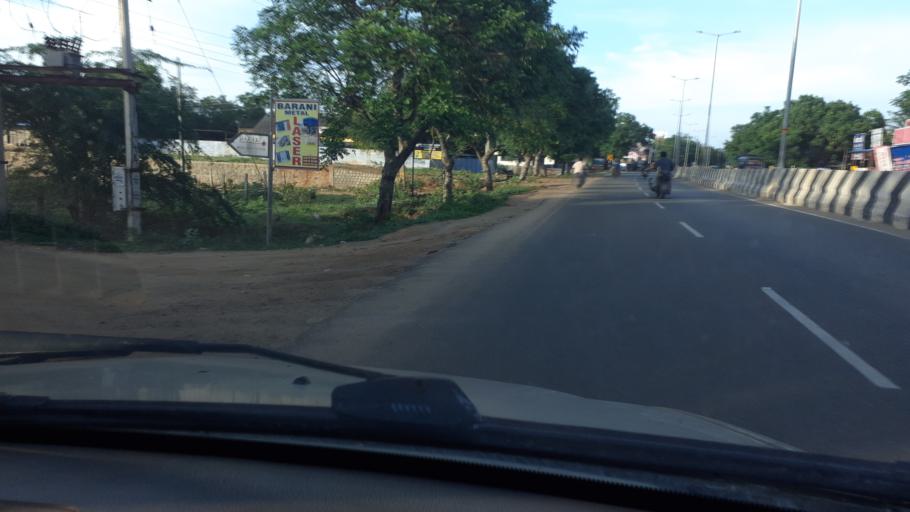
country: IN
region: Tamil Nadu
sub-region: Tirunelveli Kattabo
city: Tirunelveli
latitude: 8.6713
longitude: 77.7187
